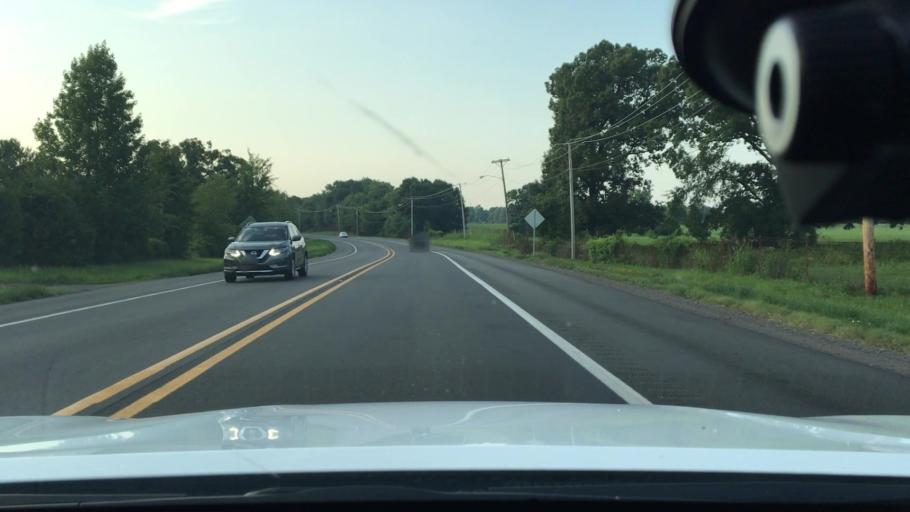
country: US
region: Arkansas
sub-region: Johnson County
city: Clarksville
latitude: 35.4557
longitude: -93.5348
